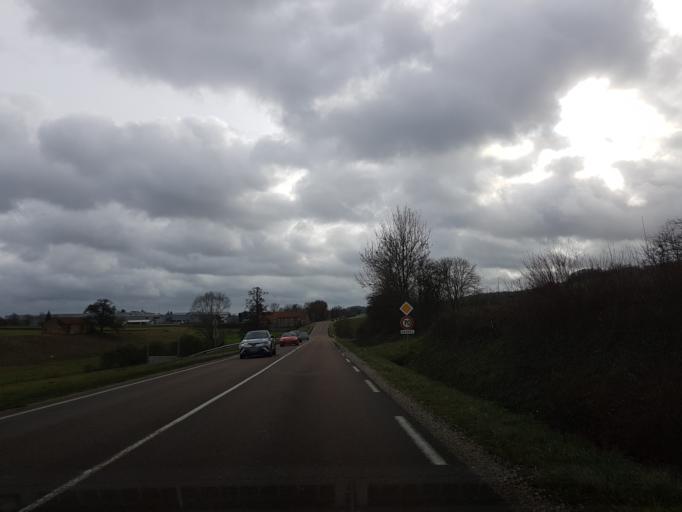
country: FR
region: Champagne-Ardenne
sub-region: Departement de la Haute-Marne
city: Langres
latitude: 47.8624
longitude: 5.3429
